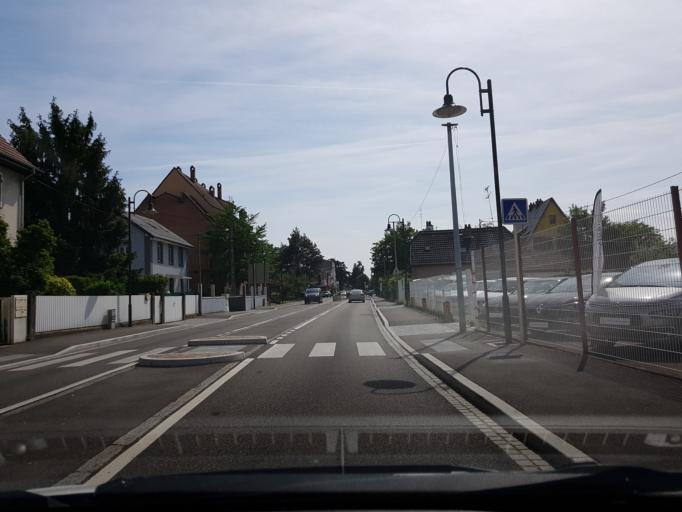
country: FR
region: Alsace
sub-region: Departement du Haut-Rhin
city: Brunstatt
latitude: 47.7277
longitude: 7.3223
